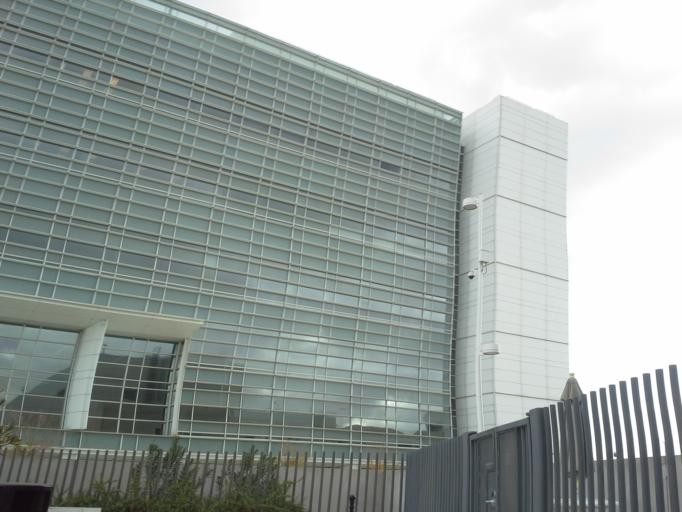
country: US
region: Arizona
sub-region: Maricopa County
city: Phoenix
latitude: 33.4477
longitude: -112.0816
